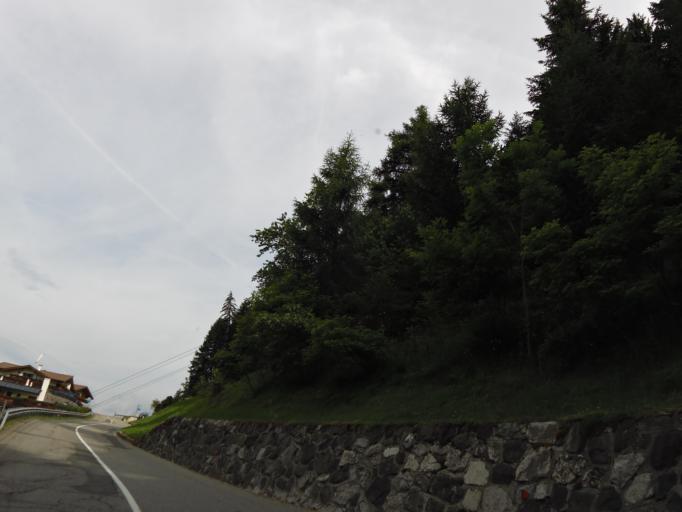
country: IT
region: Trentino-Alto Adige
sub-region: Bolzano
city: Siusi
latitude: 46.5398
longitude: 11.5888
